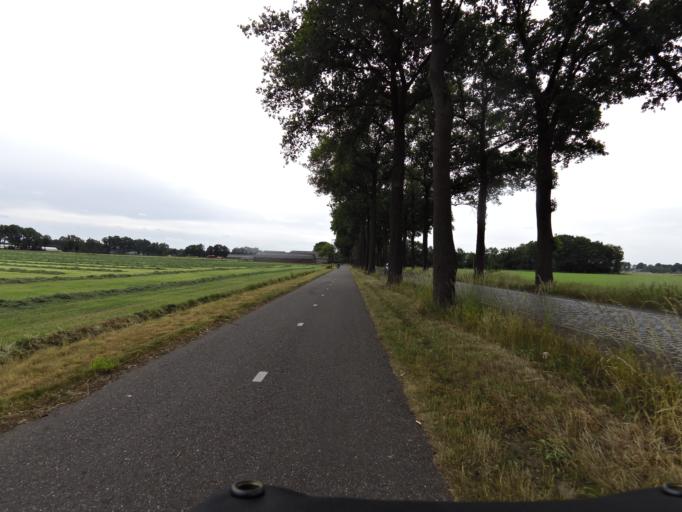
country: NL
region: North Brabant
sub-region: Gemeente Bladel en Netersel
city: Bladel
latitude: 51.3862
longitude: 5.2119
